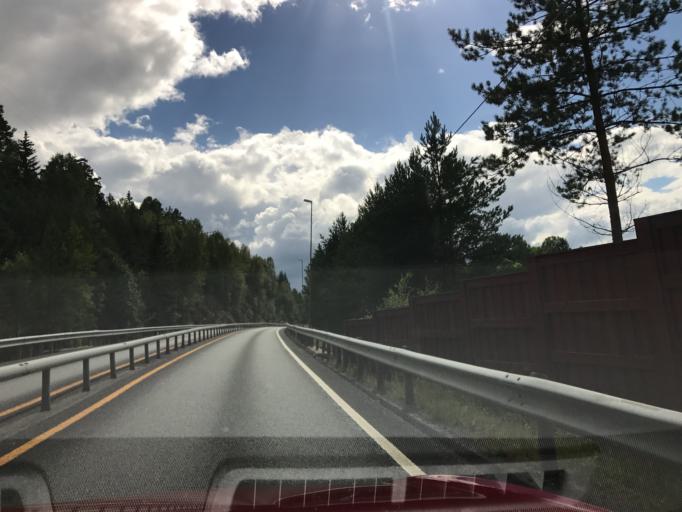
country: NO
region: Aust-Agder
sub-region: Gjerstad
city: Gjerstad
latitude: 58.8408
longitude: 9.1002
